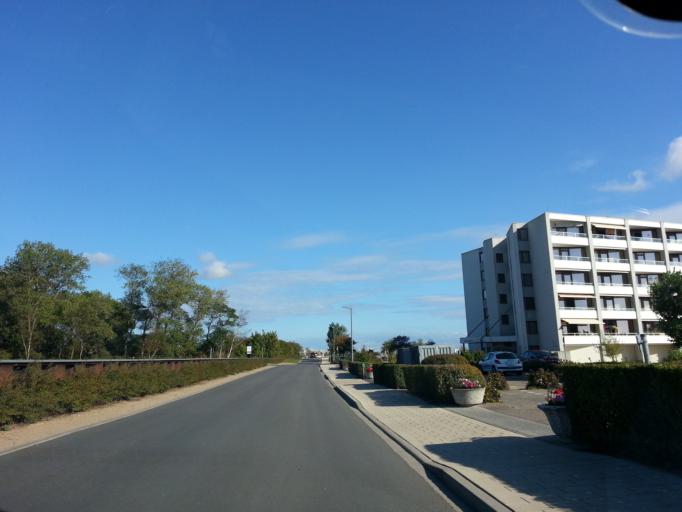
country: DE
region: Schleswig-Holstein
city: Heiligenhafen
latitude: 54.3799
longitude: 10.9677
